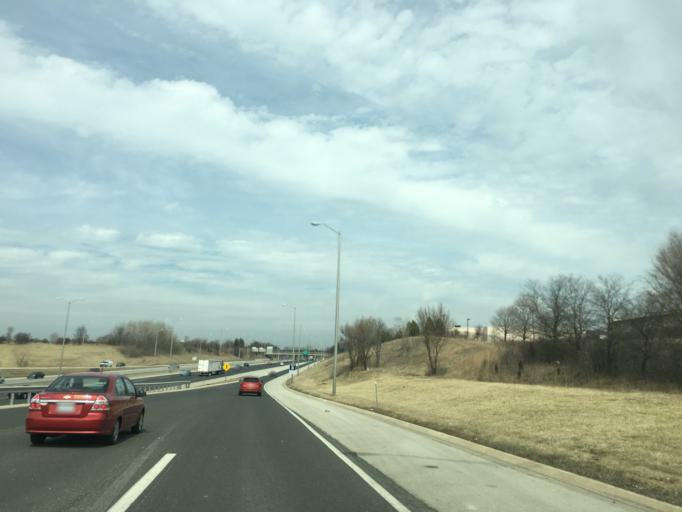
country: US
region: Illinois
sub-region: DuPage County
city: Woodridge
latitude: 41.7527
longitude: -88.0347
